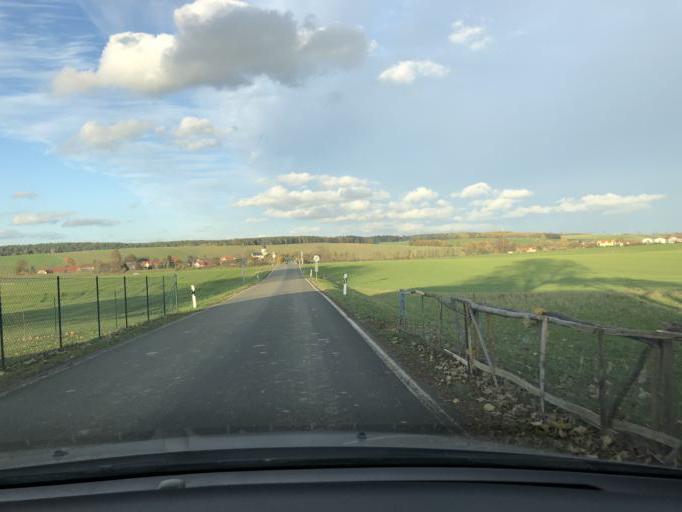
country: DE
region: Thuringia
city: Miesitz
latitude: 50.7351
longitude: 11.8203
